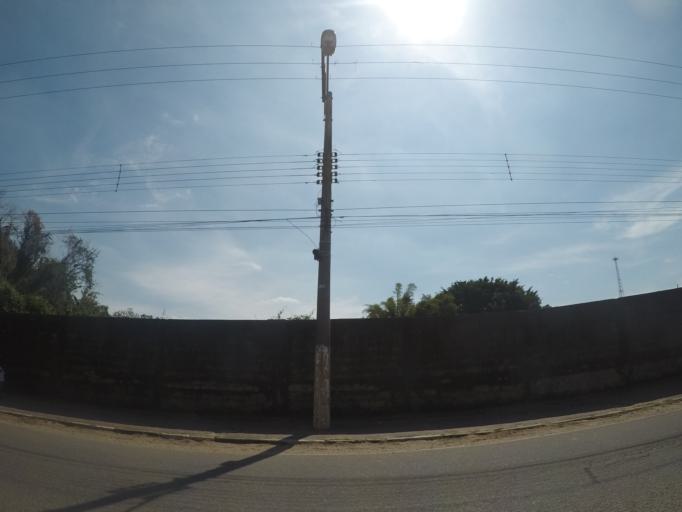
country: BR
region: Sao Paulo
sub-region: Cabreuva
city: Cabreuva
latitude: -23.2615
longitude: -47.0579
